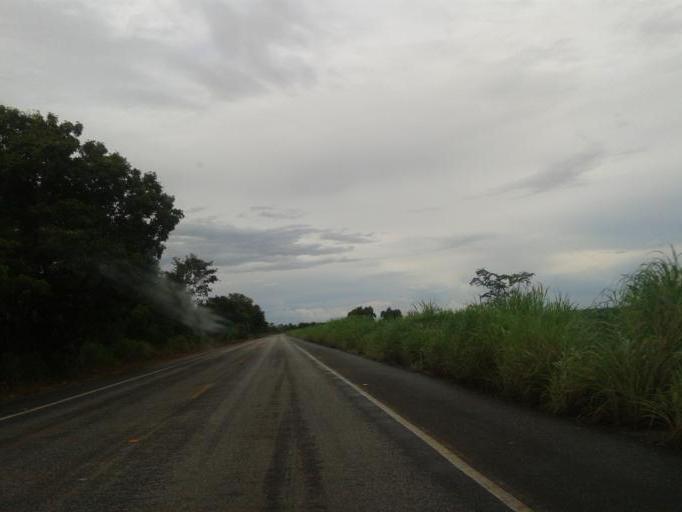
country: BR
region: Goias
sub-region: Mozarlandia
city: Mozarlandia
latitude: -14.8492
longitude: -50.5439
